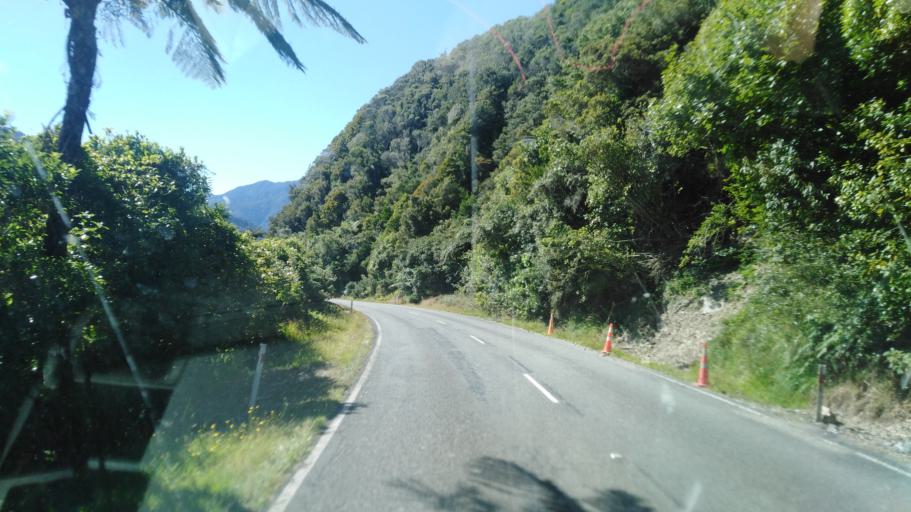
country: NZ
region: West Coast
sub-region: Buller District
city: Westport
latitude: -41.5330
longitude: 171.9553
